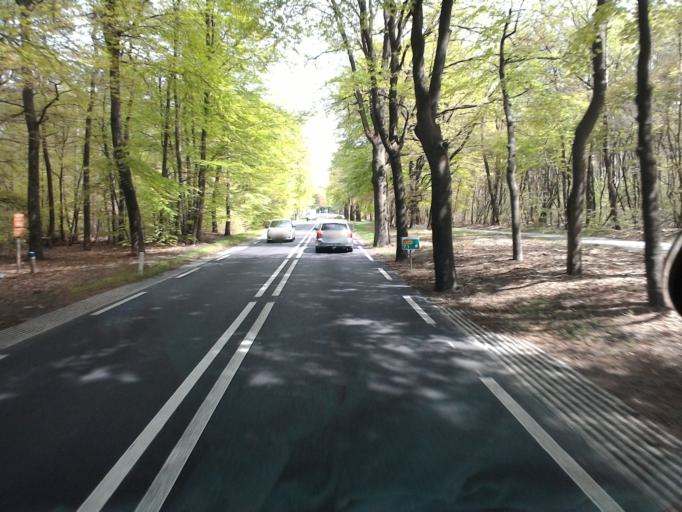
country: NL
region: Utrecht
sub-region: Gemeente Utrechtse Heuvelrug
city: Maarn
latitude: 52.0873
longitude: 5.3264
